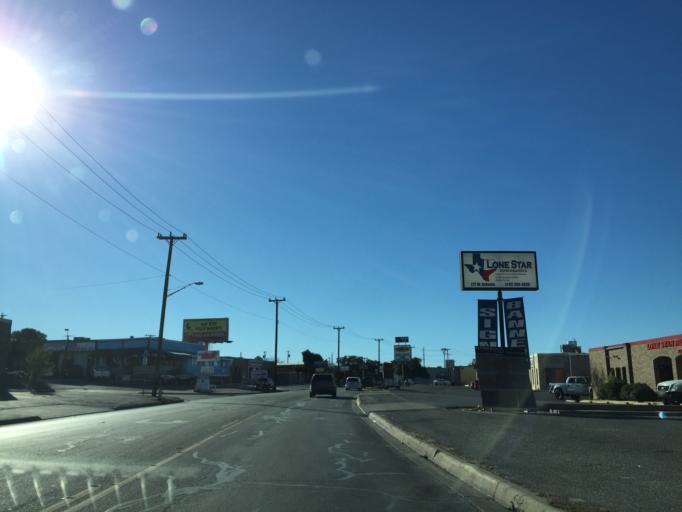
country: US
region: Texas
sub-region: Bexar County
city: Castle Hills
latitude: 29.5530
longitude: -98.4966
